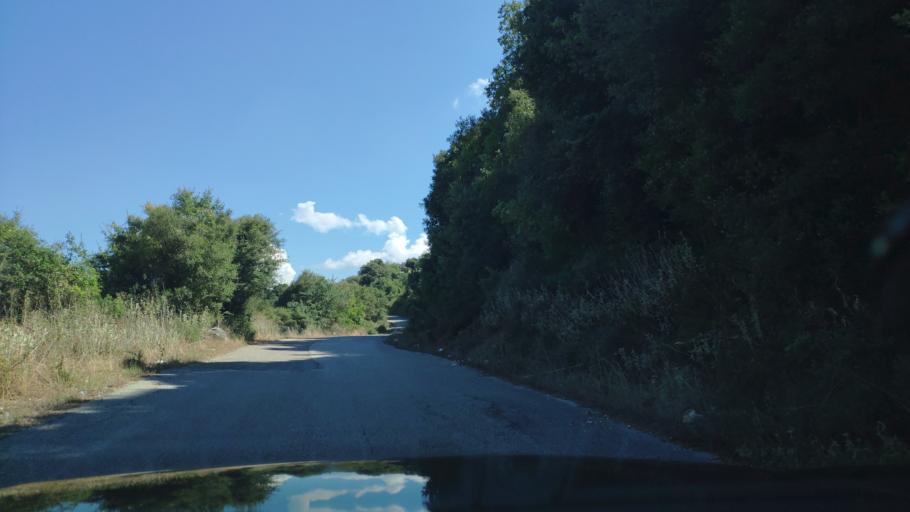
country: GR
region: West Greece
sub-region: Nomos Aitolias kai Akarnanias
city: Katouna
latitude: 38.8193
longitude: 21.1033
